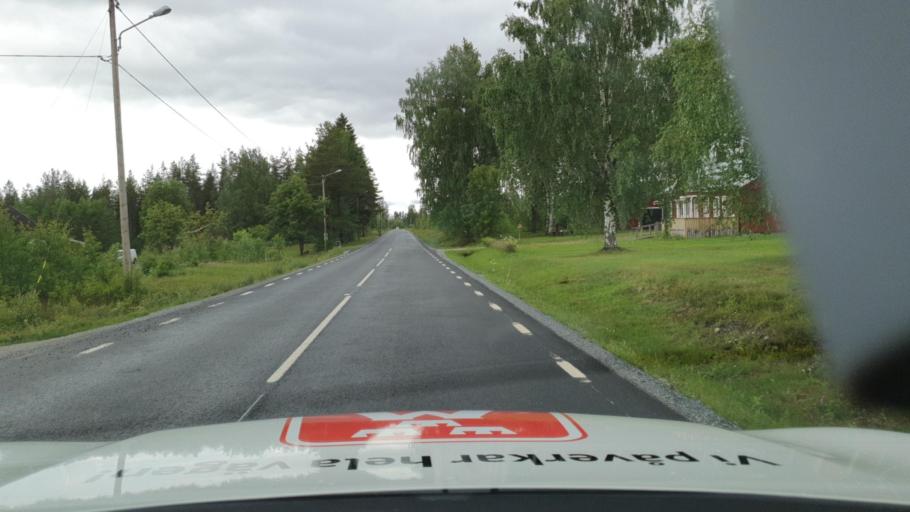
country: SE
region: Vaesterbotten
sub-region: Dorotea Kommun
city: Dorotea
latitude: 64.2132
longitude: 16.5523
